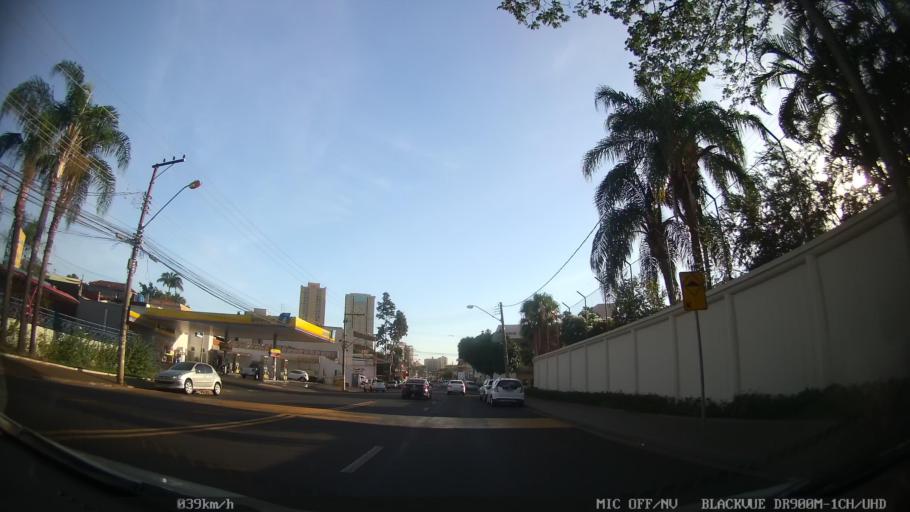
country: BR
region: Sao Paulo
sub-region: Ribeirao Preto
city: Ribeirao Preto
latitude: -21.1972
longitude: -47.8002
